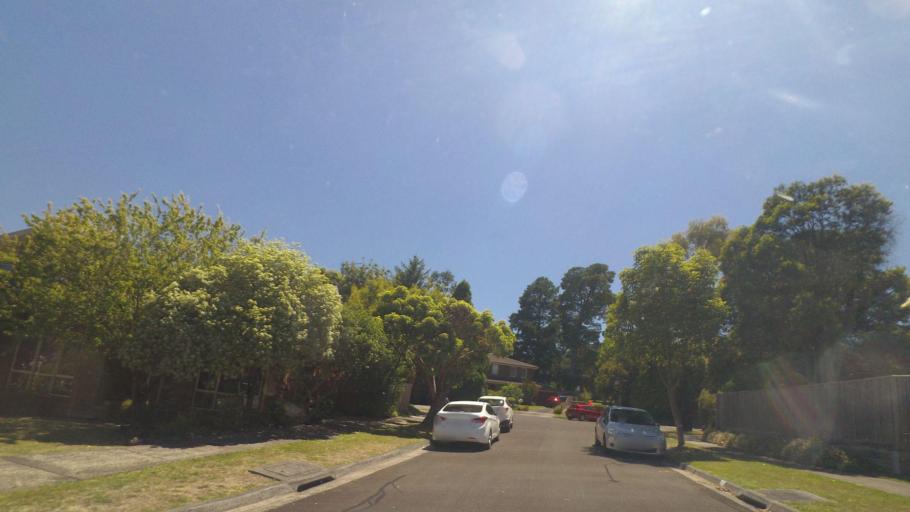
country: AU
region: Victoria
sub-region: Maroondah
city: Warranwood
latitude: -37.7908
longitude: 145.2409
